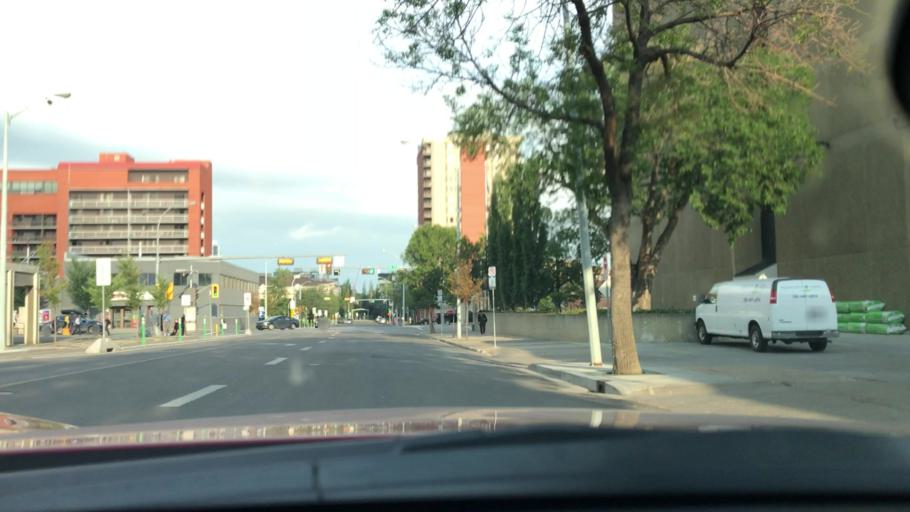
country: CA
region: Alberta
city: Edmonton
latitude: 53.5431
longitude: -113.5054
